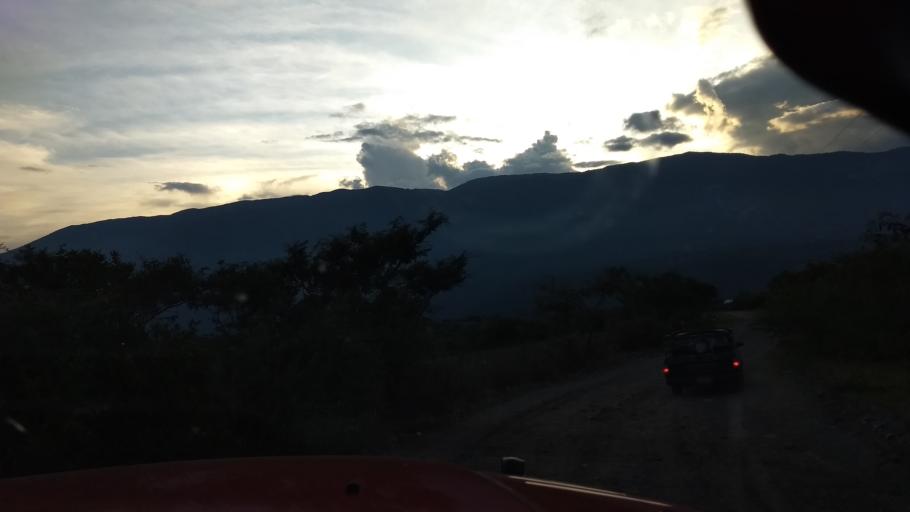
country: MX
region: Colima
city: Suchitlan
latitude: 19.4792
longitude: -103.8025
